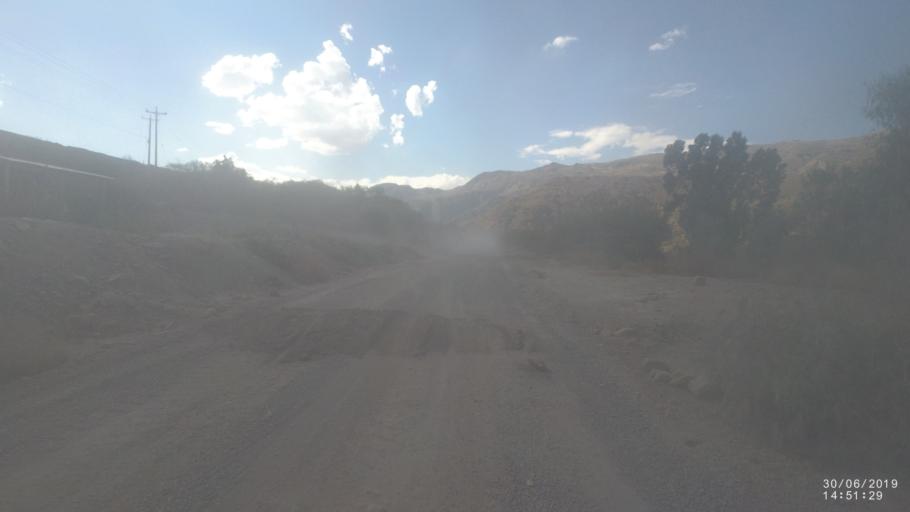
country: BO
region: Cochabamba
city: Irpa Irpa
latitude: -17.7718
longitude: -66.3435
